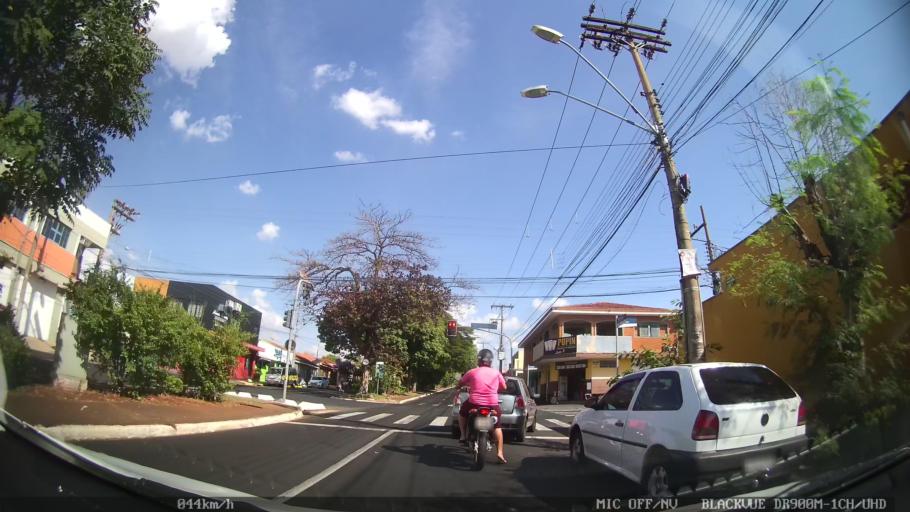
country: BR
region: Sao Paulo
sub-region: Ribeirao Preto
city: Ribeirao Preto
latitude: -21.1833
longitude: -47.8332
